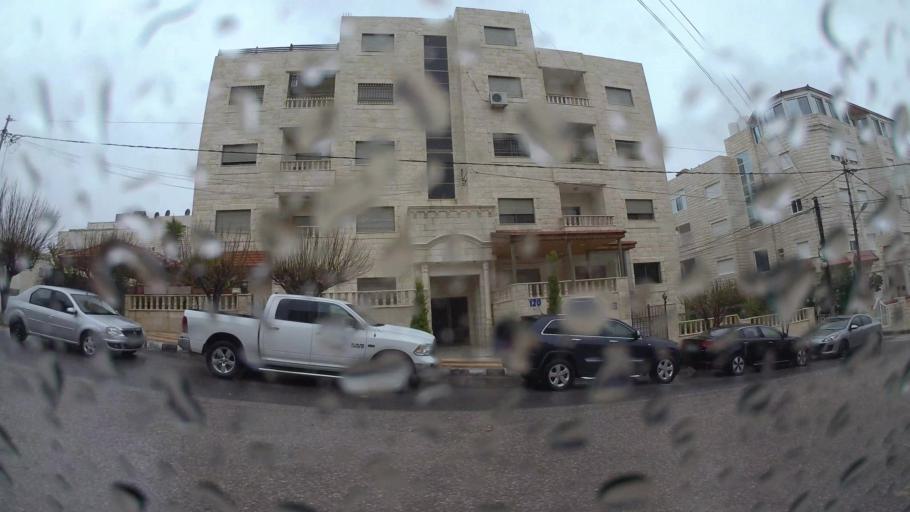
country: JO
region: Amman
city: Al Jubayhah
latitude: 32.0178
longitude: 35.8946
